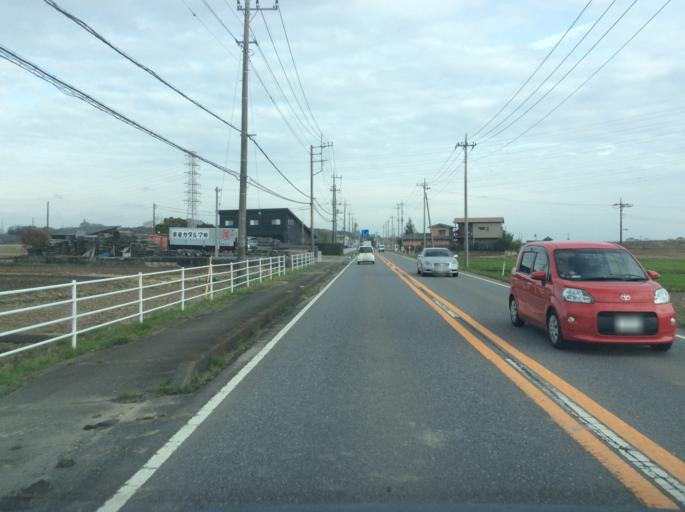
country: JP
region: Ibaraki
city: Tsukuba
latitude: 36.1379
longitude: 140.1307
